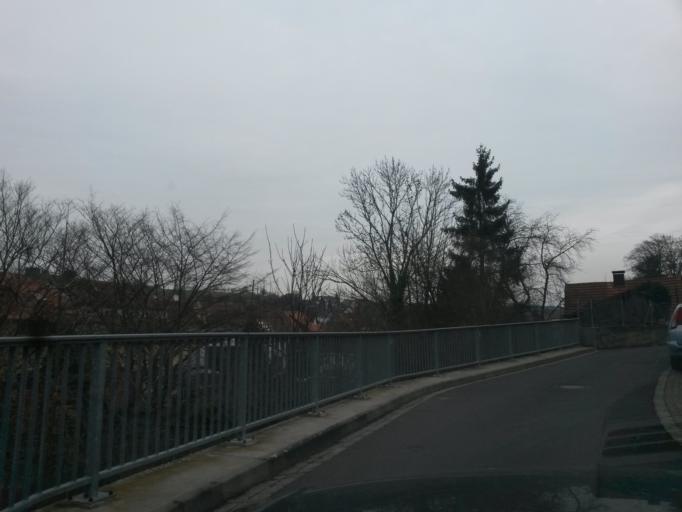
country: DE
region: Bavaria
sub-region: Regierungsbezirk Unterfranken
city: Rimpar
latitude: 49.8576
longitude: 9.9581
